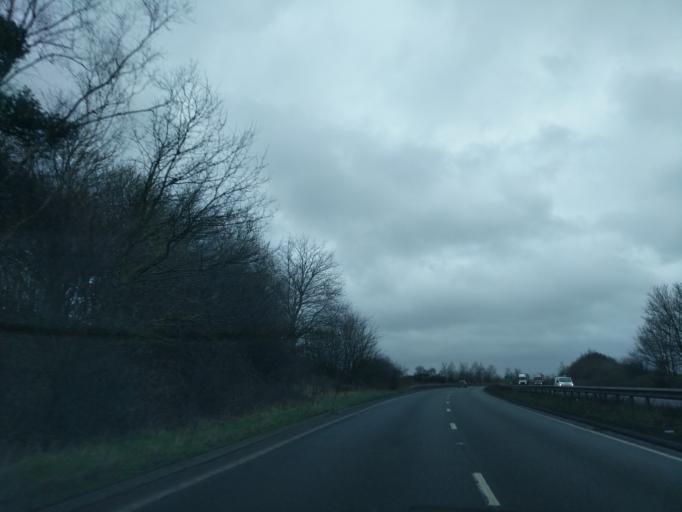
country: GB
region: England
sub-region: Staffordshire
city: Shenstone
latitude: 52.6522
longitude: -1.8237
